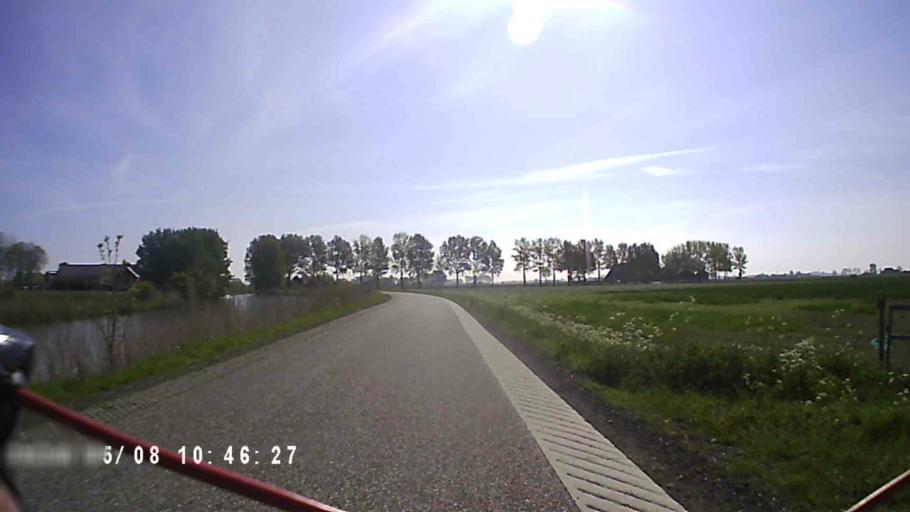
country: NL
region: Groningen
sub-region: Gemeente Winsum
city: Winsum
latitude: 53.3341
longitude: 6.5408
